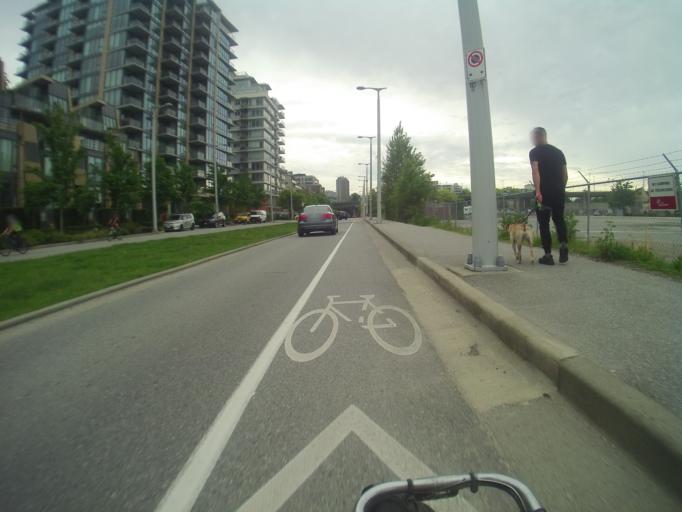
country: CA
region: British Columbia
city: Vancouver
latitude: 49.2695
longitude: -123.1115
